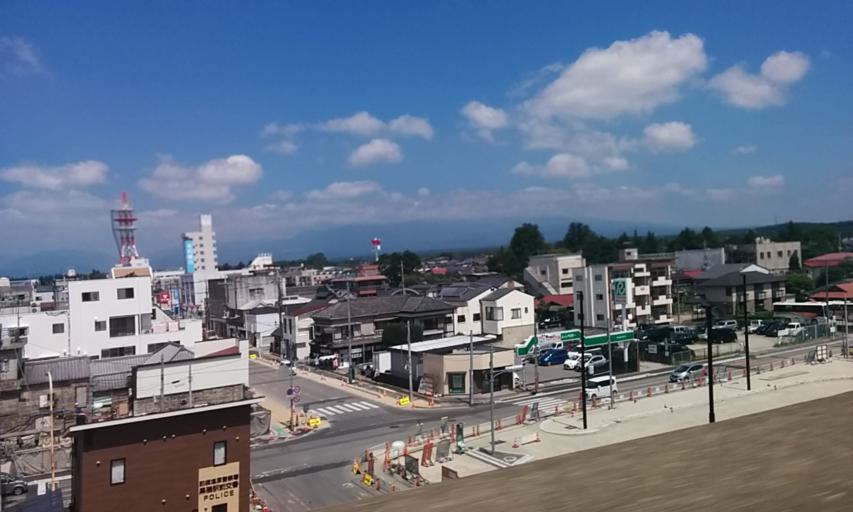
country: JP
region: Tochigi
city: Kuroiso
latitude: 36.9697
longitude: 140.0593
